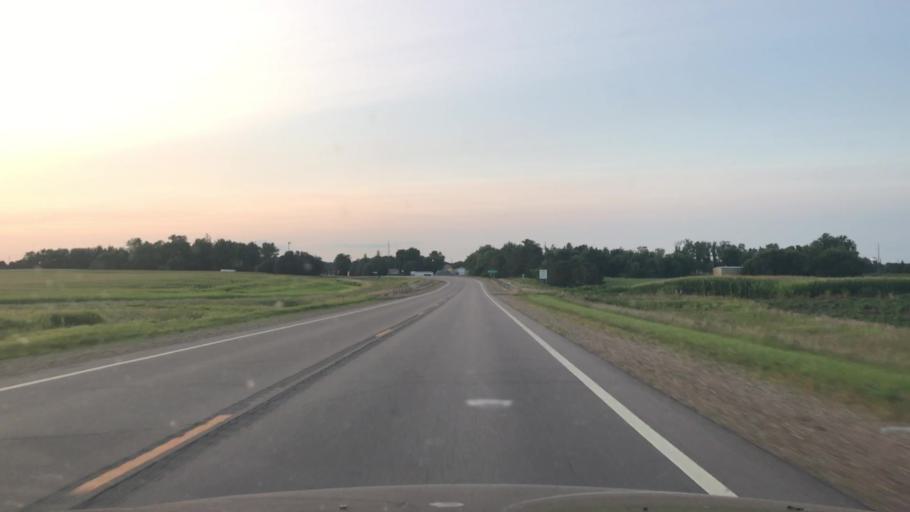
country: US
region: Minnesota
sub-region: Redwood County
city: Redwood Falls
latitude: 44.5208
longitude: -95.1180
